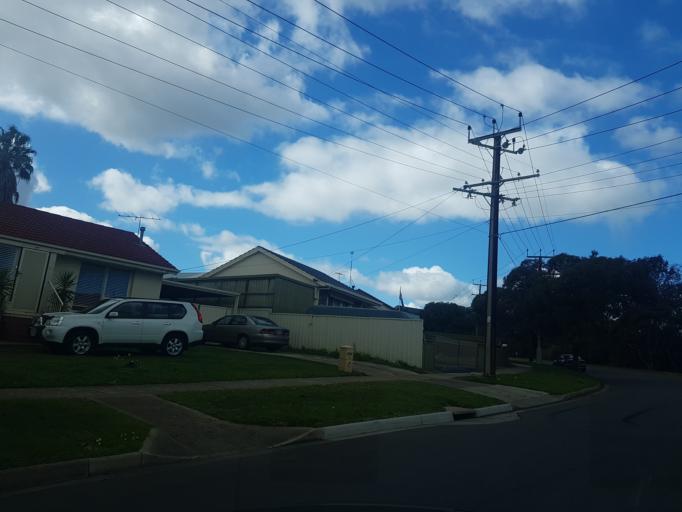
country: AU
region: South Australia
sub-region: Salisbury
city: Ingle Farm
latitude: -34.8240
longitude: 138.6440
